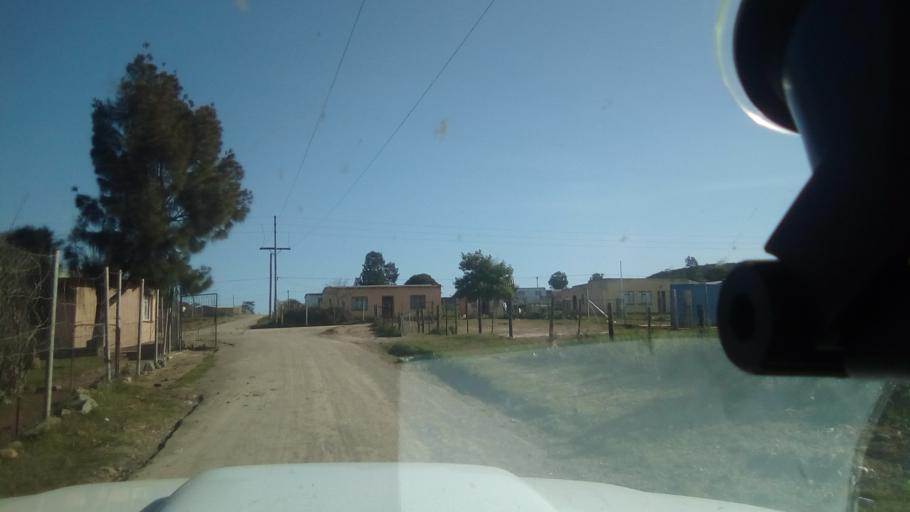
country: ZA
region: Eastern Cape
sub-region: Buffalo City Metropolitan Municipality
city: Bhisho
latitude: -32.8162
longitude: 27.3542
